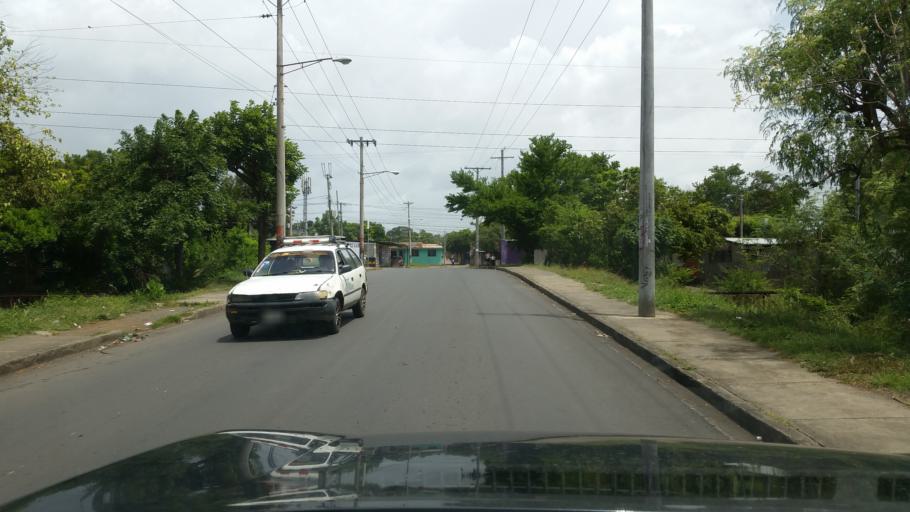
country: NI
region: Managua
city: Managua
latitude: 12.1287
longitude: -86.2131
